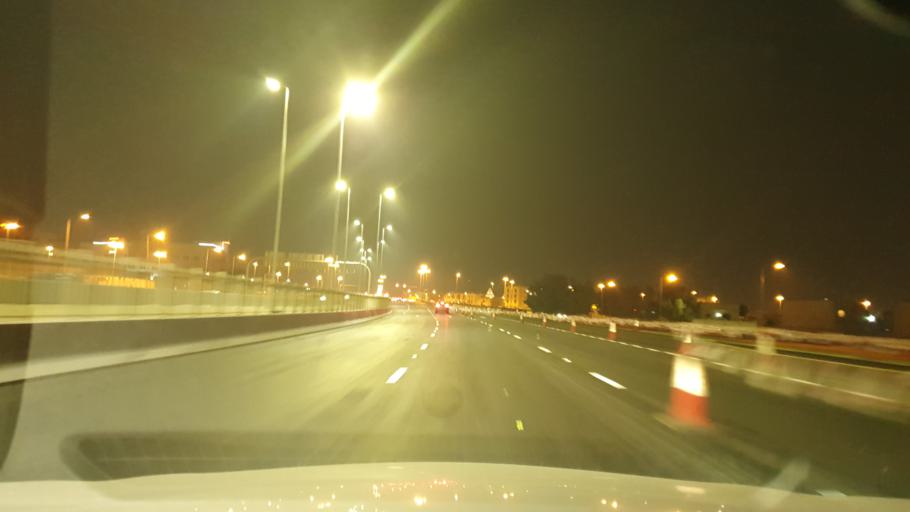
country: BH
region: Northern
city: Madinat `Isa
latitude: 26.1593
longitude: 50.5590
